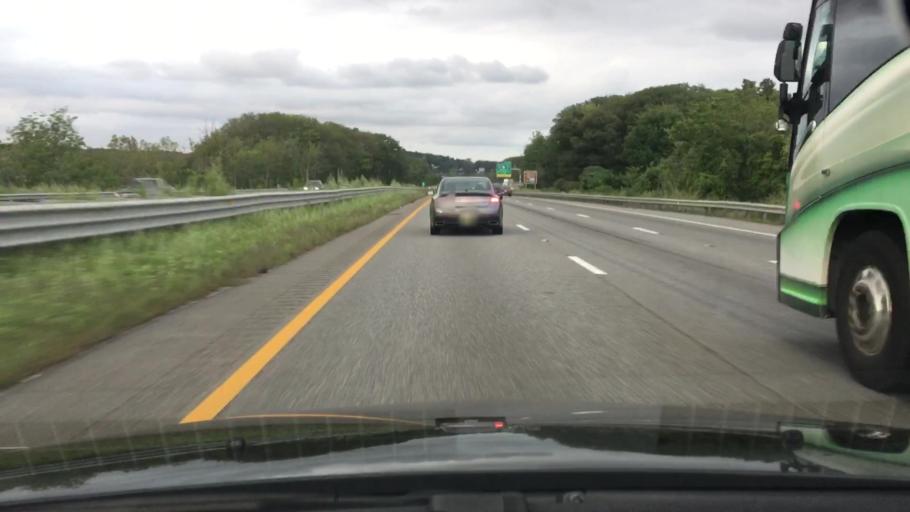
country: US
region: Massachusetts
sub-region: Worcester County
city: Auburn
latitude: 42.1887
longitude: -71.8705
